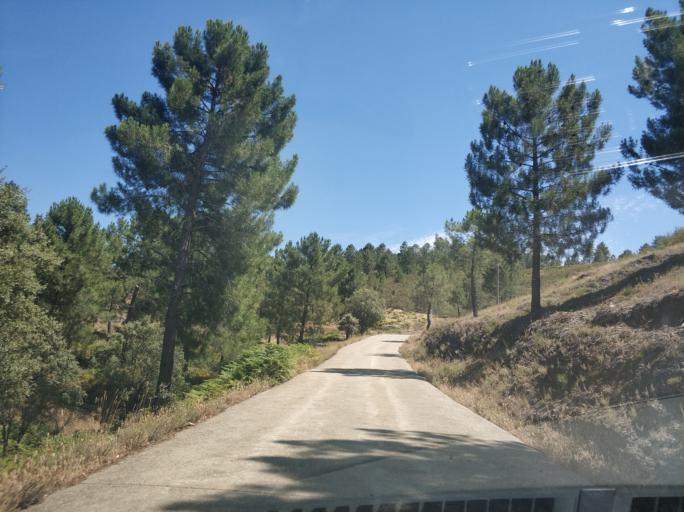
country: ES
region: Castille and Leon
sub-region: Provincia de Salamanca
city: Herguijuela de la Sierra
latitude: 40.4002
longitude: -6.0778
